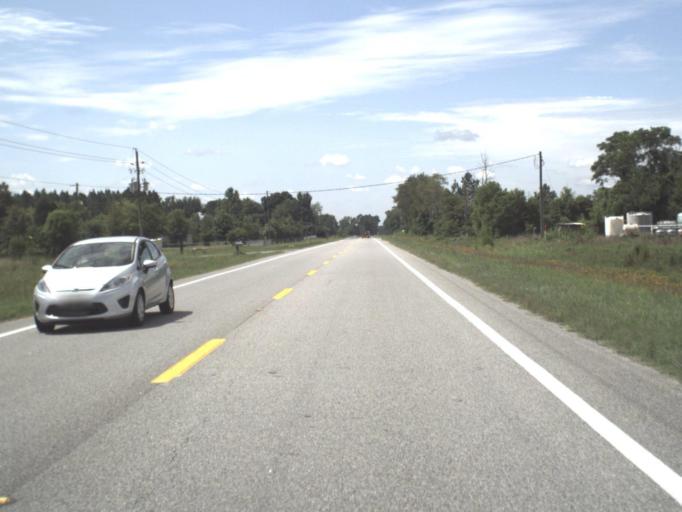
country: US
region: Florida
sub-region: Hamilton County
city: Jasper
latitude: 30.4181
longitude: -82.9337
